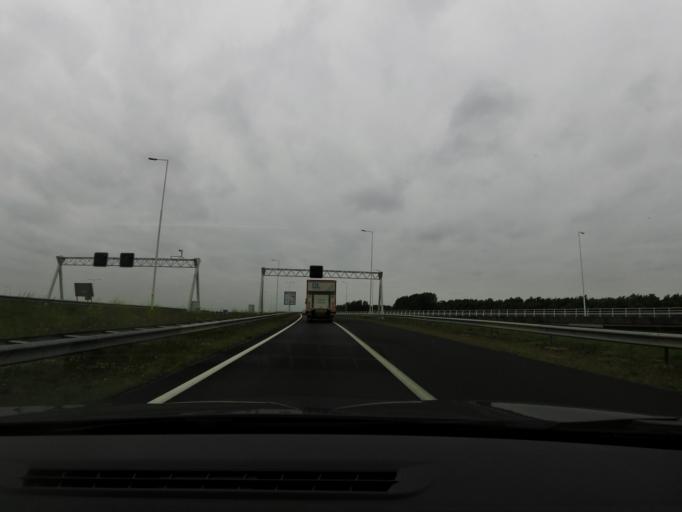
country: NL
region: South Holland
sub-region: Gemeente Barendrecht
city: Barendrecht
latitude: 51.8663
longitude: 4.5129
